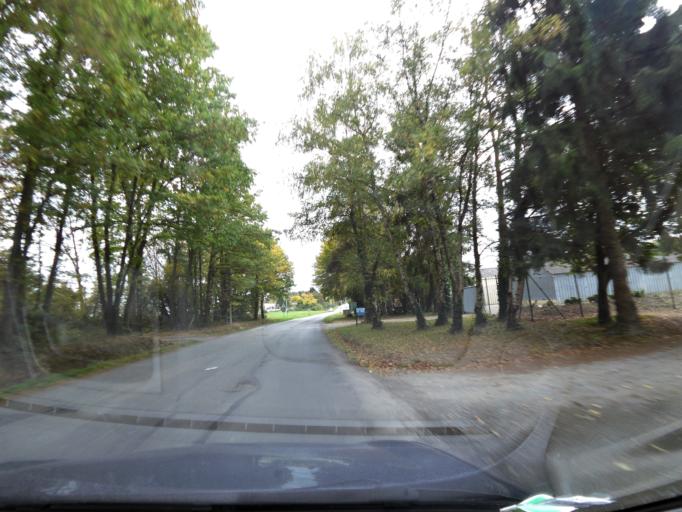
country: FR
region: Brittany
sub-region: Departement d'Ille-et-Vilaine
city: Vern-sur-Seiche
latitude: 48.0615
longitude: -1.6034
